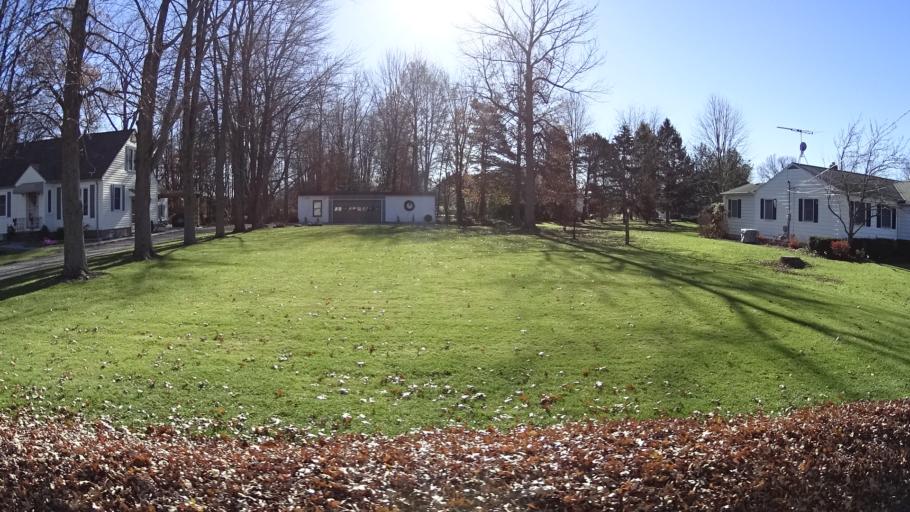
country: US
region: Ohio
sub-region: Lorain County
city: Avon
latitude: 41.4427
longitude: -82.0294
